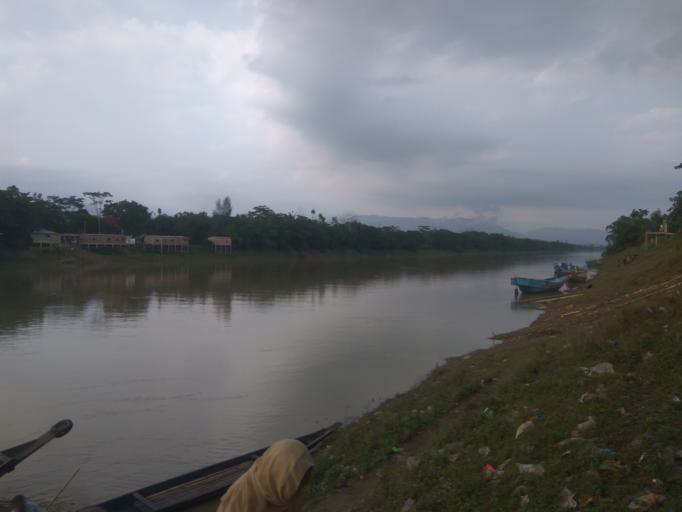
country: IN
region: Assam
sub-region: Karimganj
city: Karimganj
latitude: 24.9875
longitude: 92.4001
